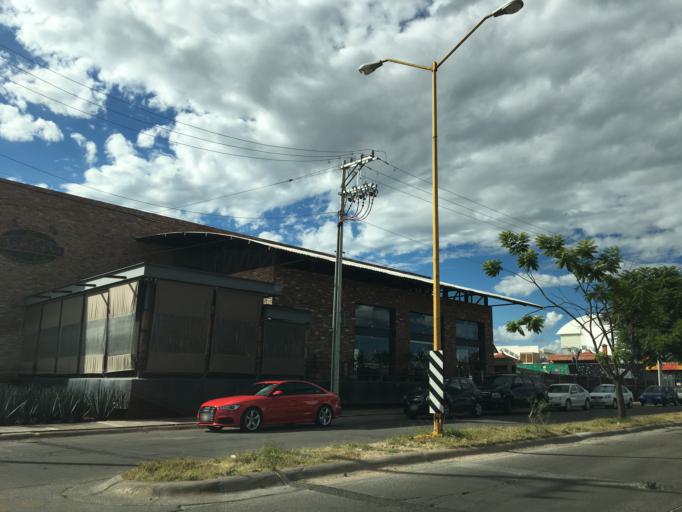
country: MX
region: Aguascalientes
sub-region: Jesus Maria
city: El Llano
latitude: 21.9251
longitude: -102.3015
